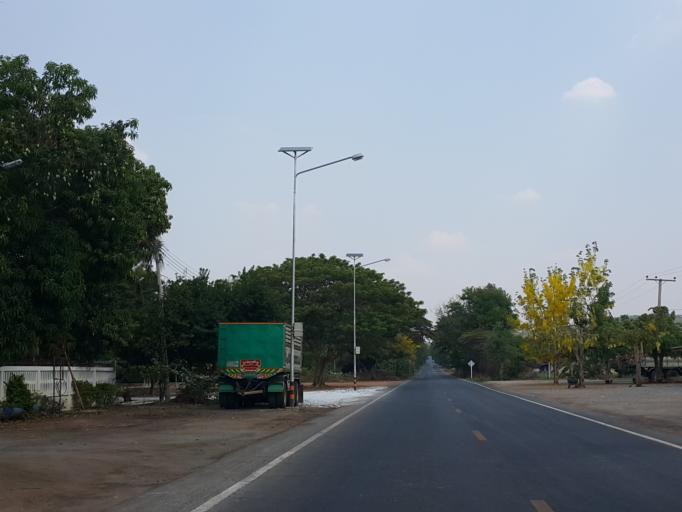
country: TH
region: Kanchanaburi
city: Nong Prue
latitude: 14.5410
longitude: 99.5793
